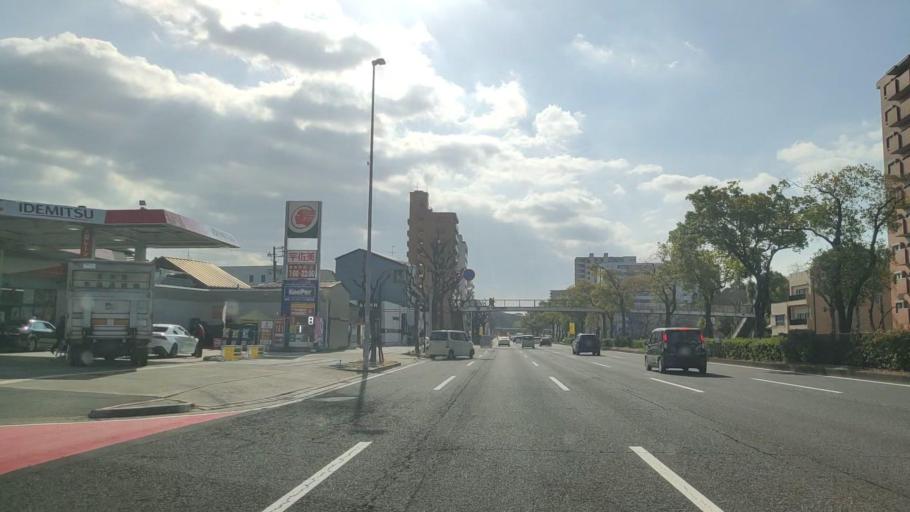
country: JP
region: Aichi
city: Nagoya-shi
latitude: 35.1328
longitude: 136.9033
